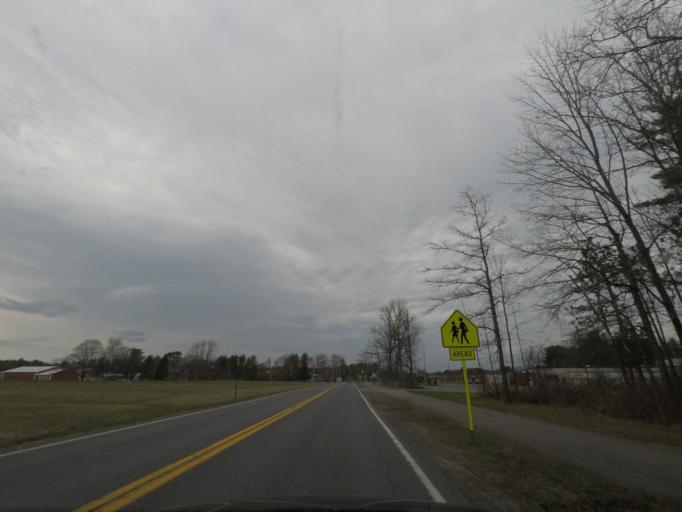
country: US
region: New York
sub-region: Albany County
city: Delmar
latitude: 42.6068
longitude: -73.8557
